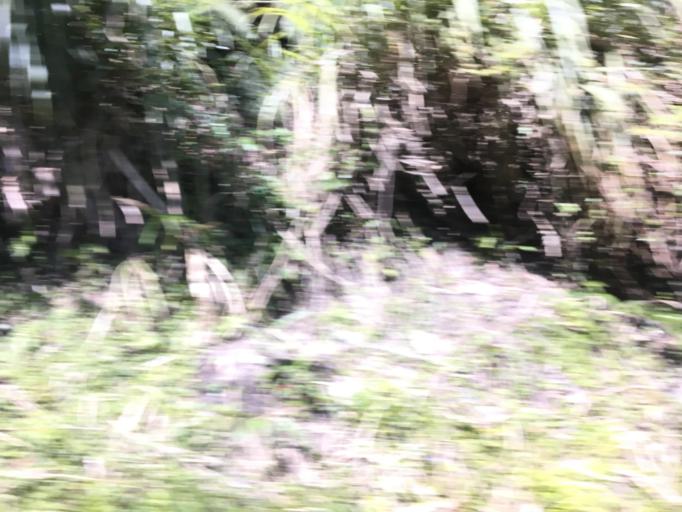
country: TW
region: Taiwan
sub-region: Yilan
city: Yilan
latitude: 24.5381
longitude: 121.5172
